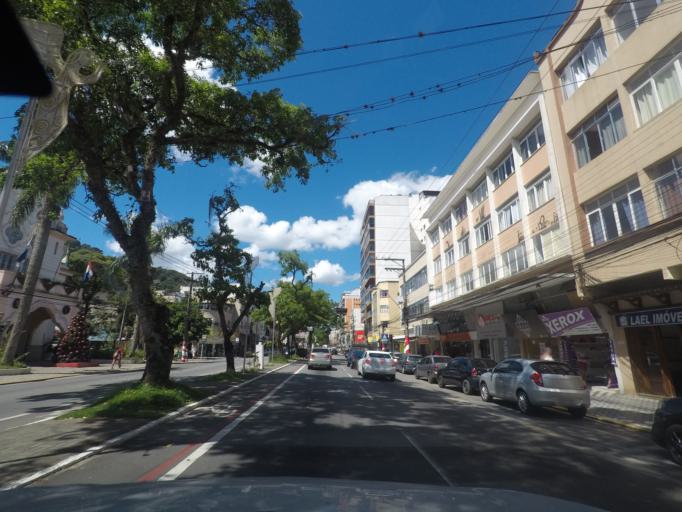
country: BR
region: Rio de Janeiro
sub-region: Teresopolis
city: Teresopolis
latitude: -22.4184
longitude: -42.9737
